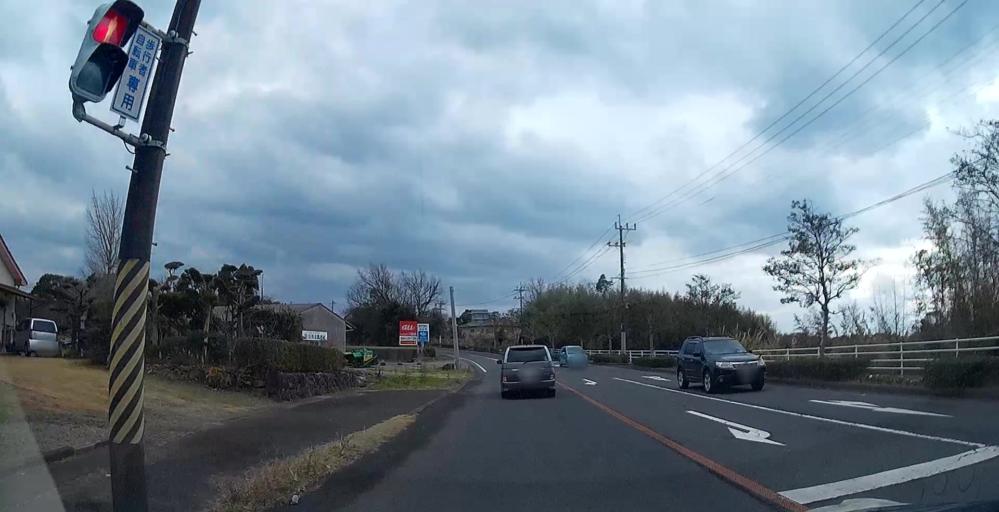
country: JP
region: Kagoshima
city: Akune
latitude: 32.0790
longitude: 130.2050
